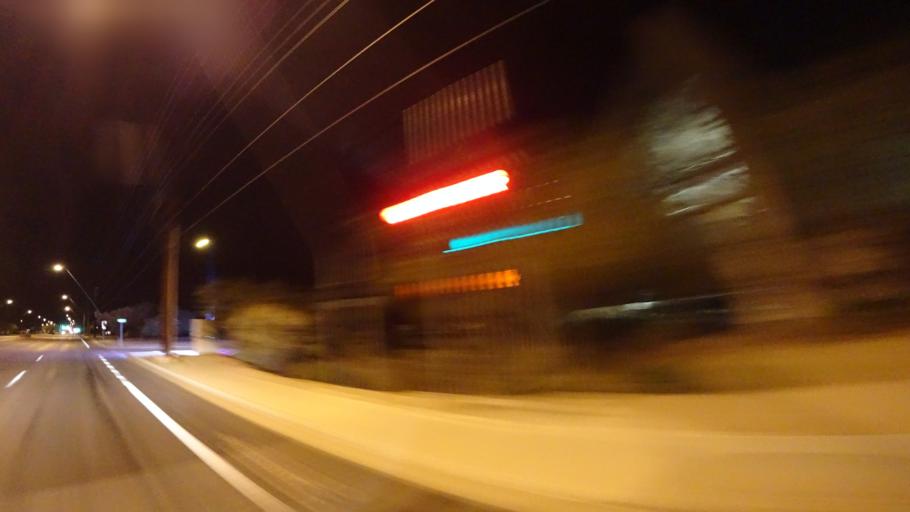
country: US
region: Arizona
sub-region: Pinal County
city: Apache Junction
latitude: 33.4447
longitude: -111.6841
